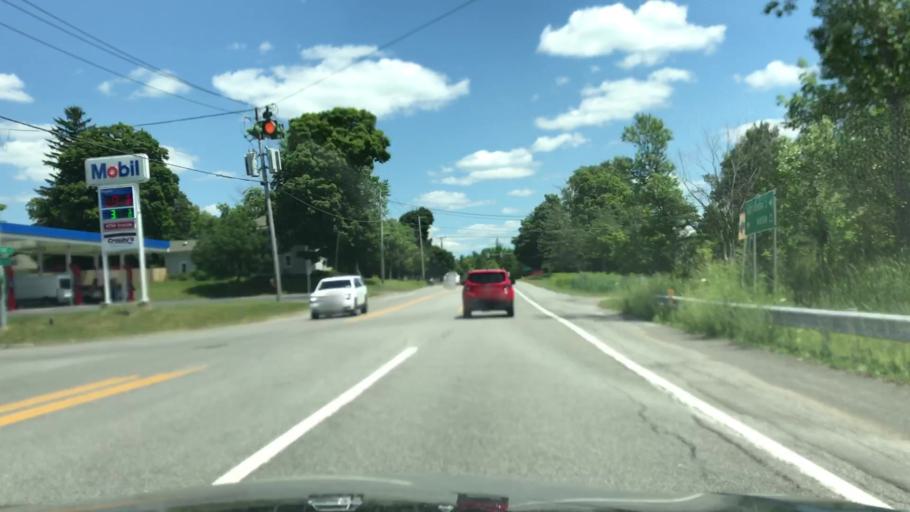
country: US
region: New York
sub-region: Erie County
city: East Aurora
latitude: 42.7679
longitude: -78.5530
